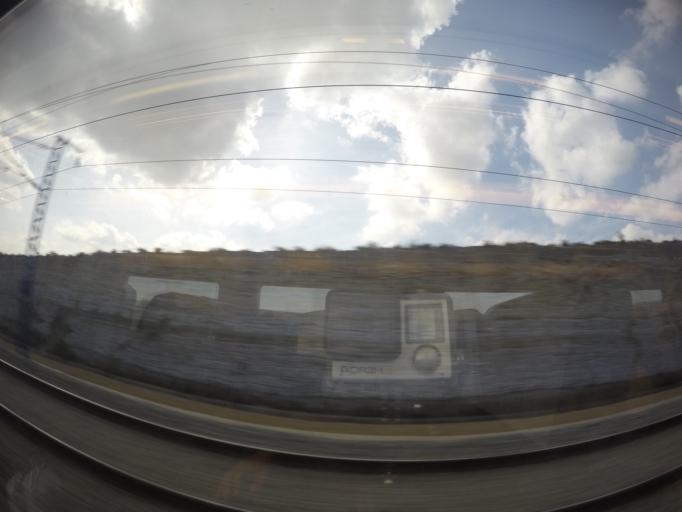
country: ES
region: Aragon
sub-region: Provincia de Zaragoza
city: Fuentes de Ebro
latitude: 41.4986
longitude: -0.6586
